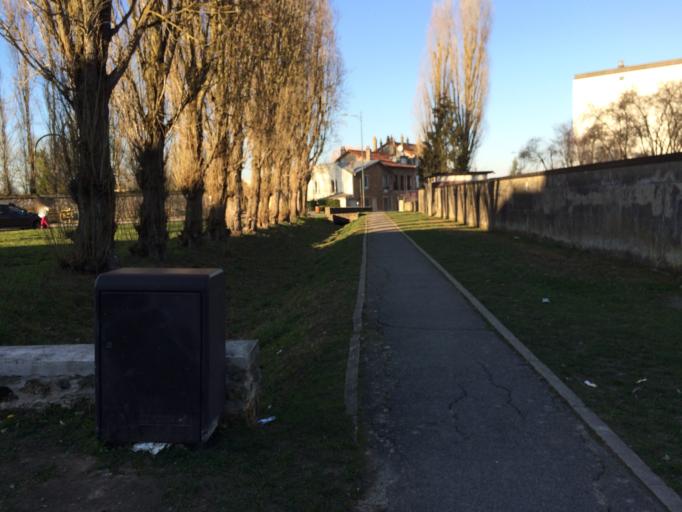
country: FR
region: Ile-de-France
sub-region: Departement de l'Essonne
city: Villebon-sur-Yvette
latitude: 48.7157
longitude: 2.2378
